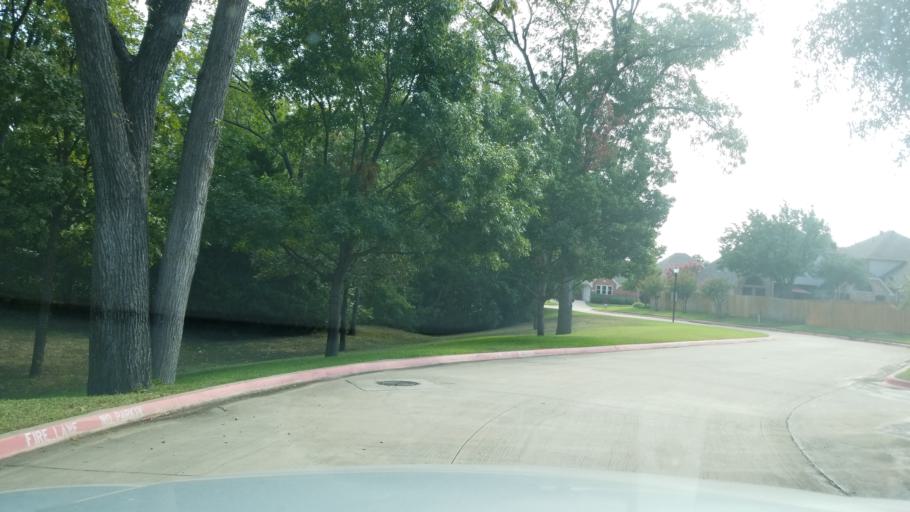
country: US
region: Texas
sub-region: Tarrant County
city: Euless
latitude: 32.8459
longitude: -97.0811
